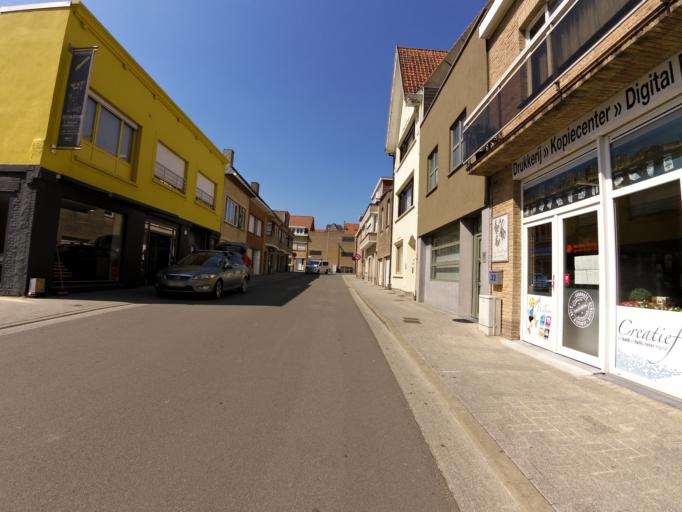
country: BE
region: Flanders
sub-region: Provincie West-Vlaanderen
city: Middelkerke
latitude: 51.1874
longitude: 2.8210
